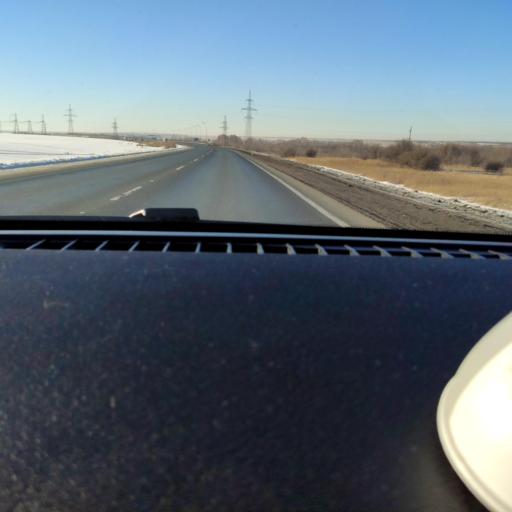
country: RU
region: Samara
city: Smyshlyayevka
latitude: 53.1422
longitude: 50.4412
